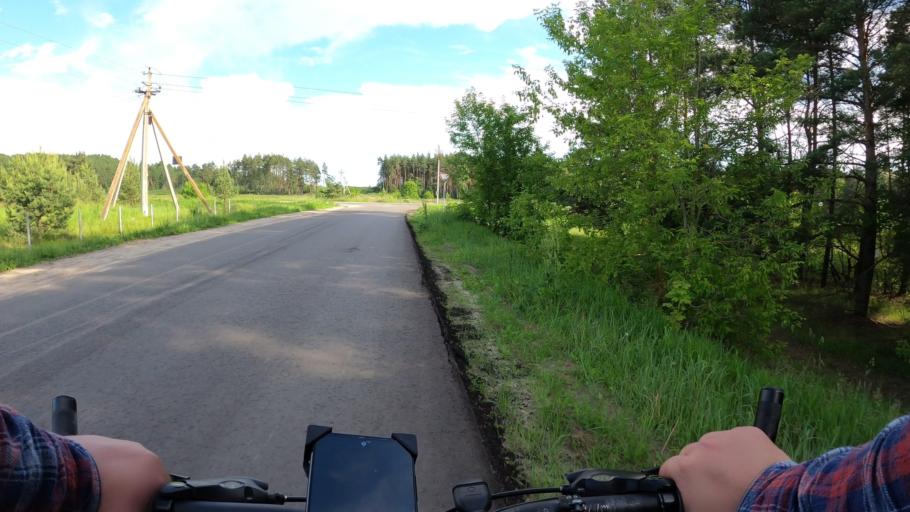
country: RU
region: Moskovskaya
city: Konobeyevo
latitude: 55.4363
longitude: 38.6338
